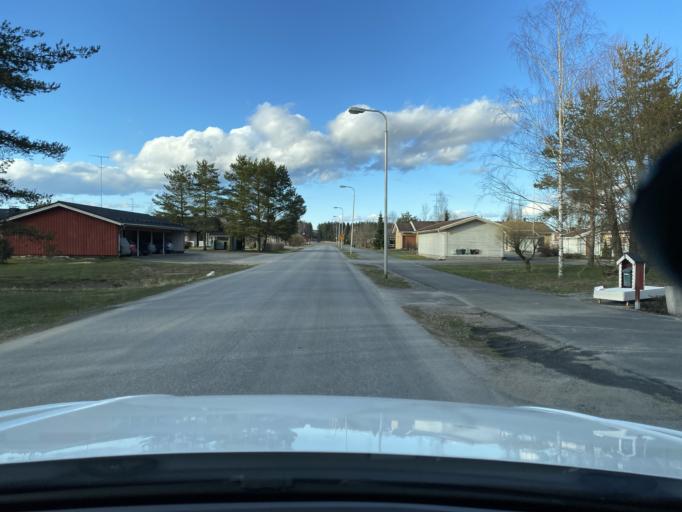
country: FI
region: Pirkanmaa
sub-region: Lounais-Pirkanmaa
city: Punkalaidun
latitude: 61.1160
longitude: 23.1106
